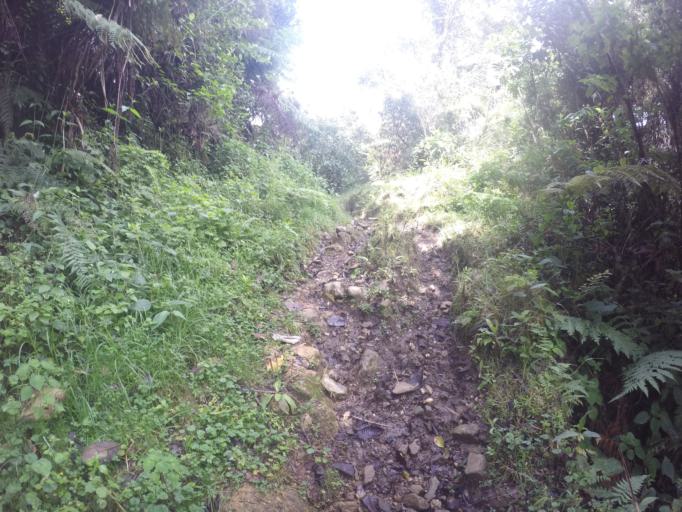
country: CO
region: Tolima
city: Cajamarca
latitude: 4.5353
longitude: -75.3475
